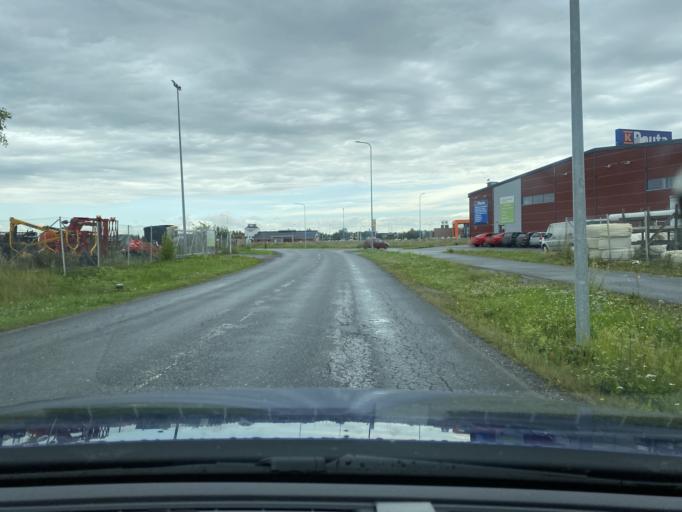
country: FI
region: Satakunta
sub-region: Pori
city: Huittinen
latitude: 61.1727
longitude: 22.6819
